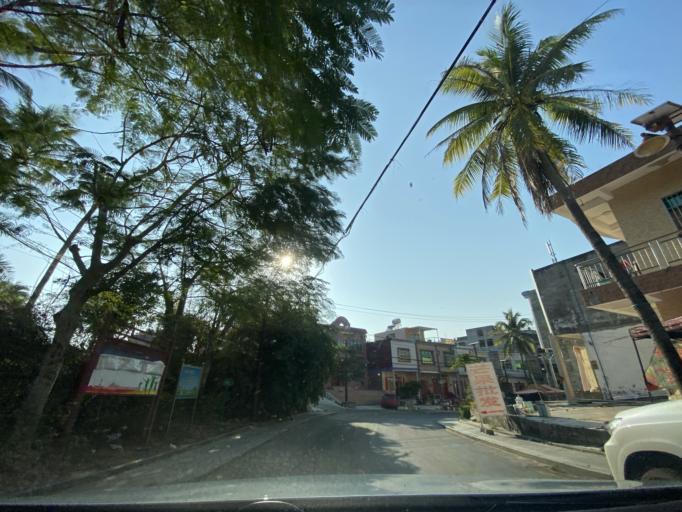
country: CN
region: Hainan
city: Yingzhou
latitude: 18.3870
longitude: 109.8201
